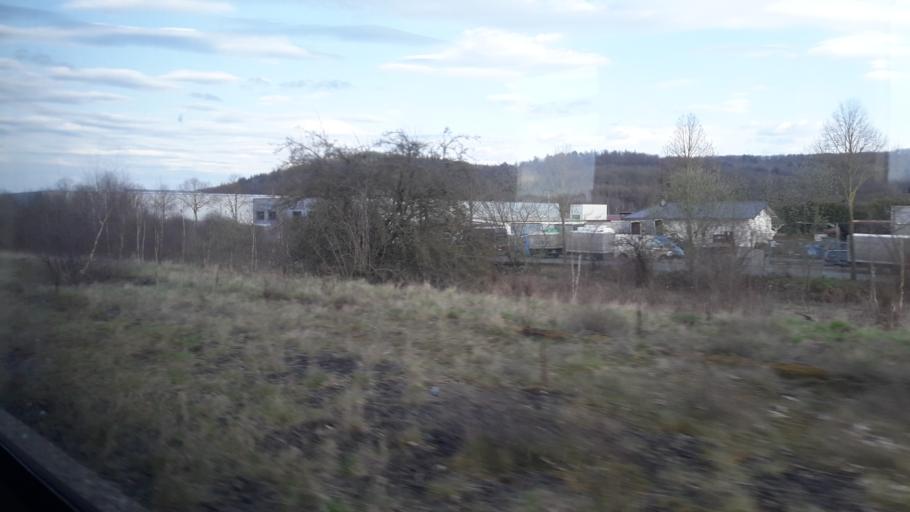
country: DE
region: North Rhine-Westphalia
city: Marsberg
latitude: 51.4964
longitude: 8.9171
